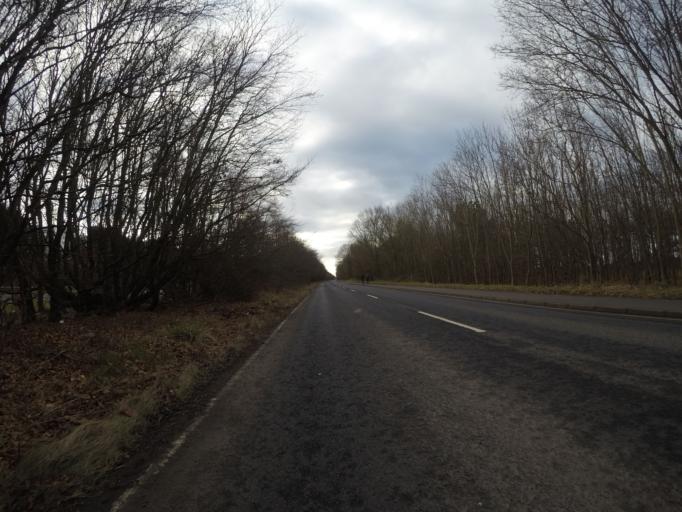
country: GB
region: Scotland
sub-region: North Ayrshire
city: Dreghorn
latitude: 55.5830
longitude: -4.6455
